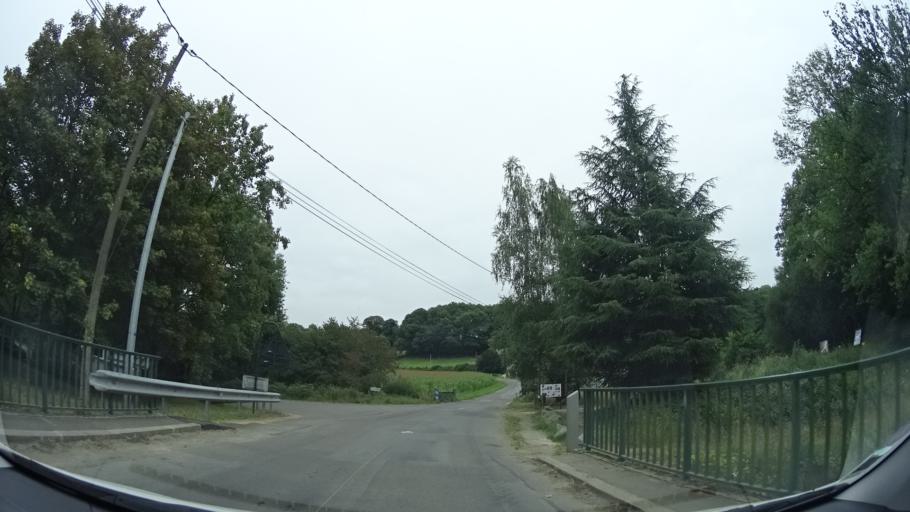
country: FR
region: Brittany
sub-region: Departement d'Ille-et-Vilaine
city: Hede-Bazouges
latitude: 48.3016
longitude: -1.7718
